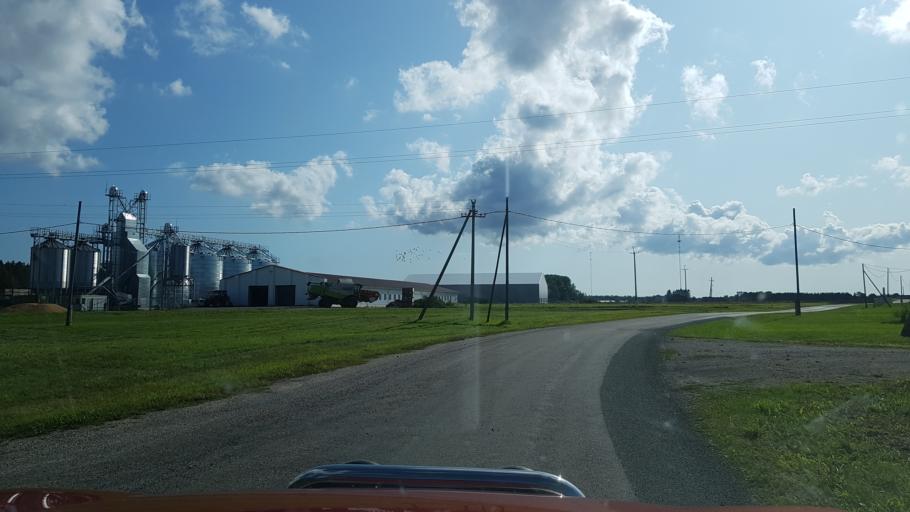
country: EE
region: Harju
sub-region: Paldiski linn
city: Paldiski
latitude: 59.2353
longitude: 24.0194
